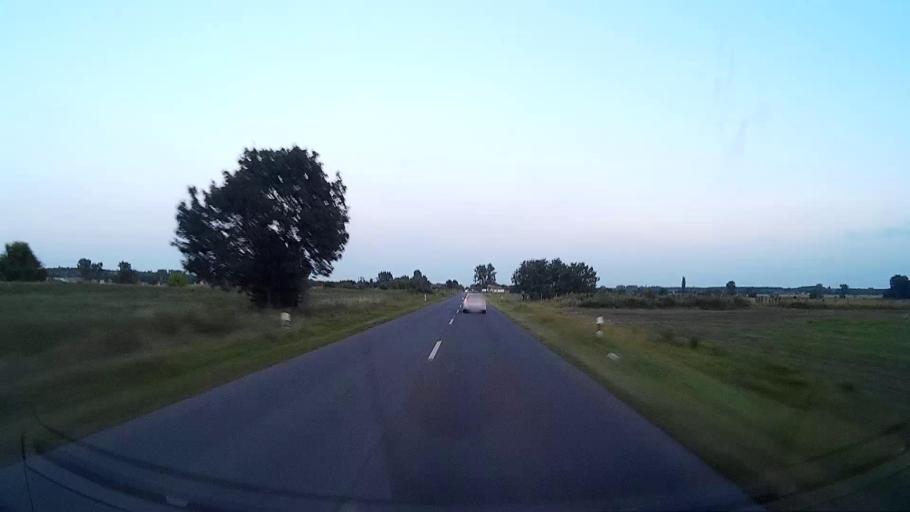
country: HU
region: Pest
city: Cegledbercel
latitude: 47.2311
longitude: 19.6561
